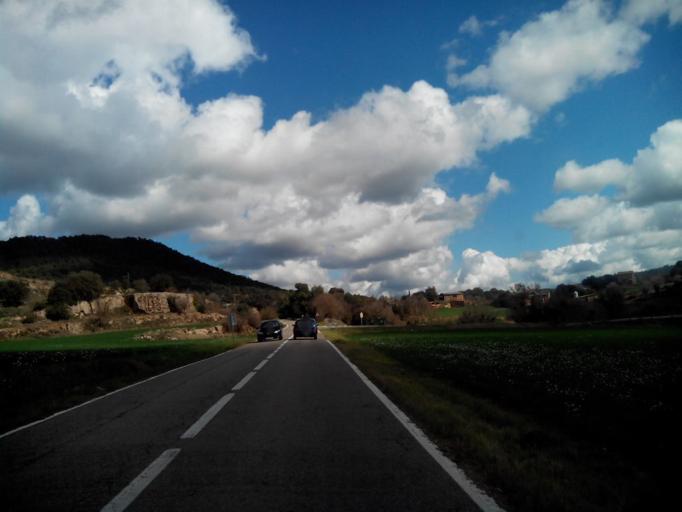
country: ES
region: Catalonia
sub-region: Provincia de Barcelona
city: Cardona
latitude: 41.9317
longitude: 1.6919
